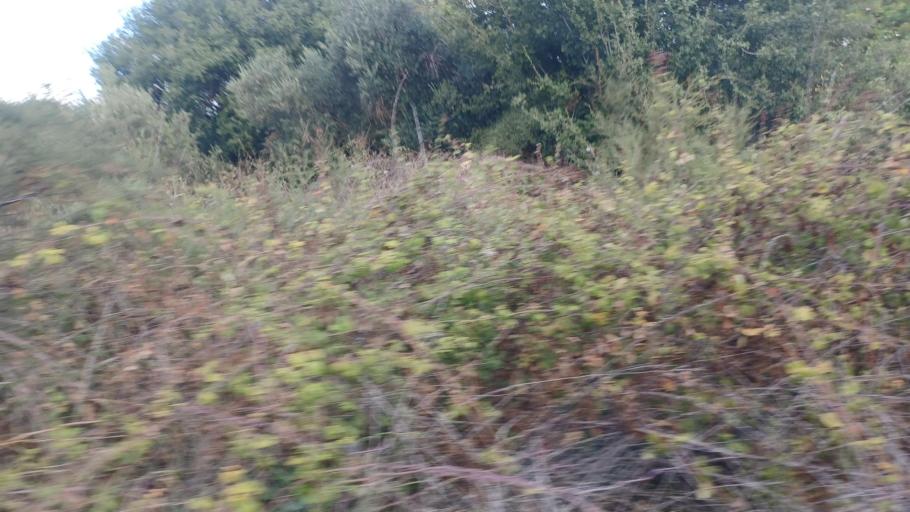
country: CY
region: Pafos
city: Mesogi
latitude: 34.8449
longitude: 32.5433
